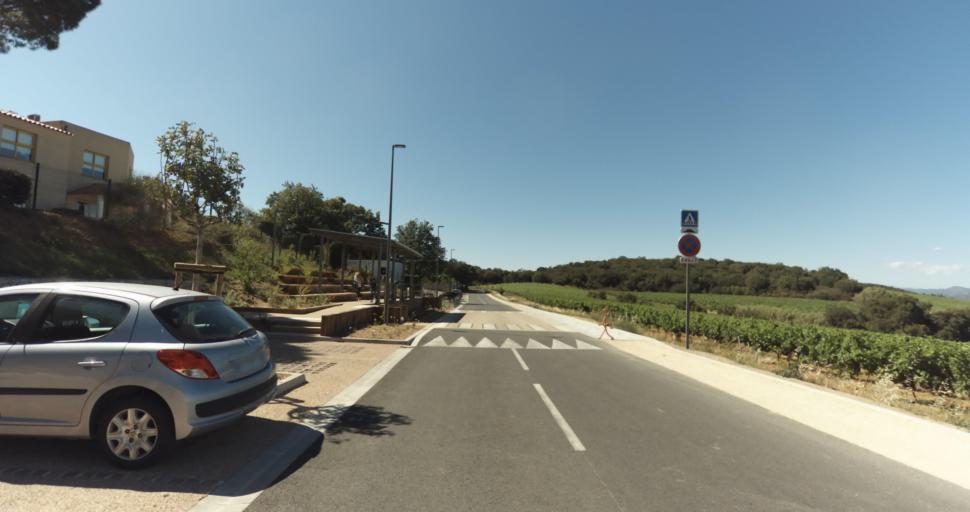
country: FR
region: Provence-Alpes-Cote d'Azur
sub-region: Departement du Var
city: La Croix-Valmer
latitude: 43.2132
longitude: 6.5615
